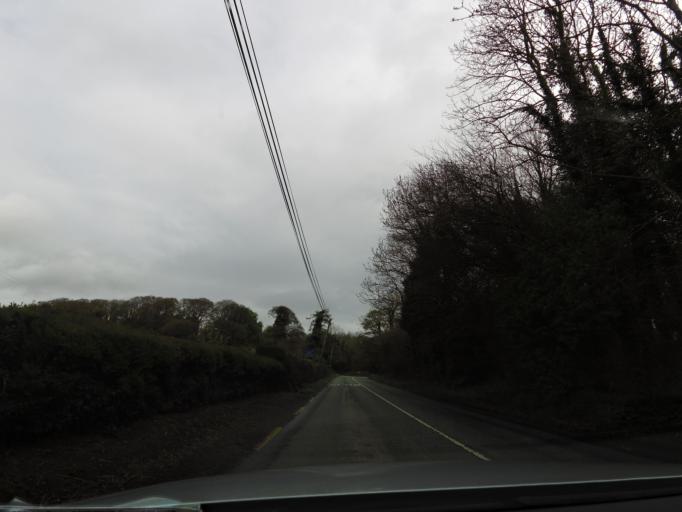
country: IE
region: Leinster
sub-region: Kilkenny
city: Ballyragget
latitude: 52.7308
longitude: -7.4539
